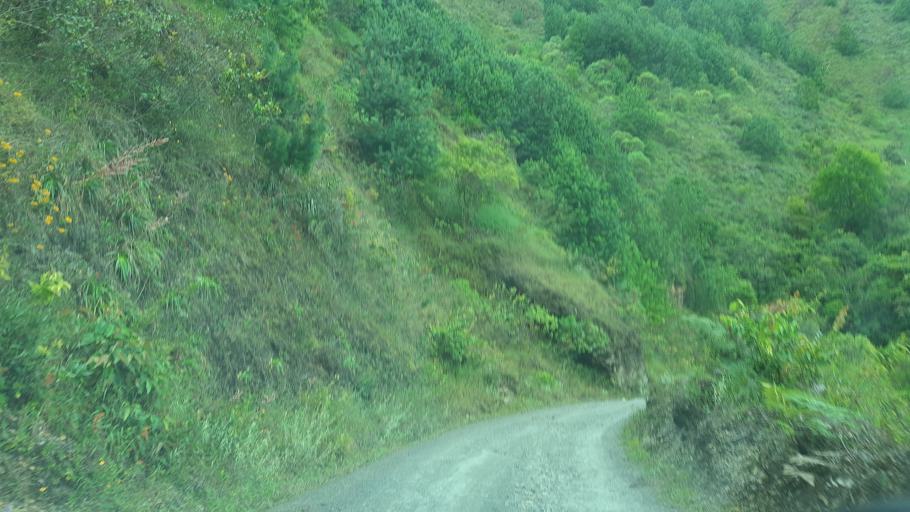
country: CO
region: Boyaca
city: Garagoa
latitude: 5.0006
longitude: -73.3332
